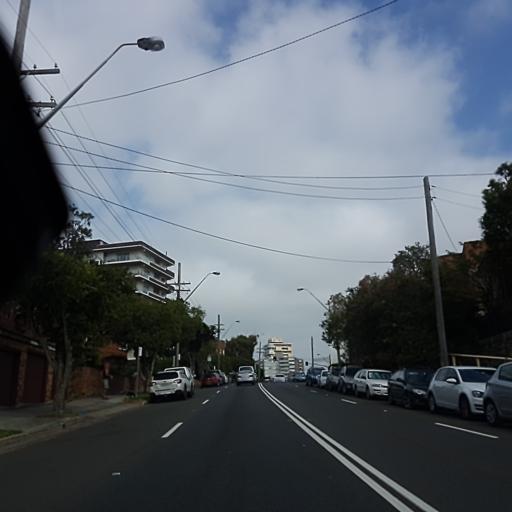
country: AU
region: New South Wales
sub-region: Manly Vale
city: Fairlight
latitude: -33.7959
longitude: 151.2789
